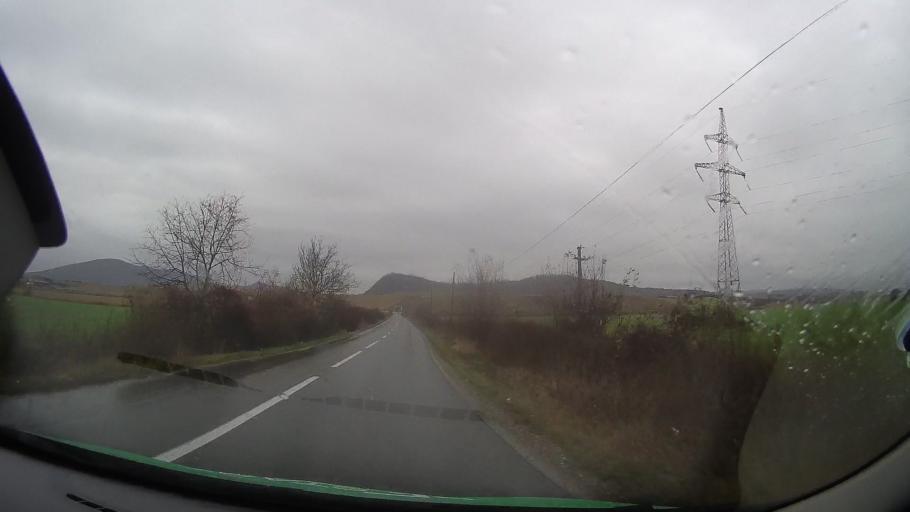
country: RO
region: Bistrita-Nasaud
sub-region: Municipiul Bistrita
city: Viisoara
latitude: 47.0526
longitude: 24.4505
